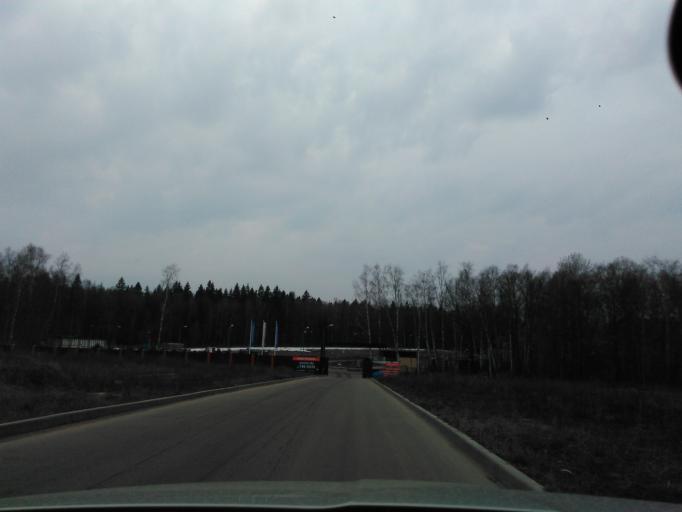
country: RU
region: Moskovskaya
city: Chashnikovo
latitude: 56.0357
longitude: 37.1514
